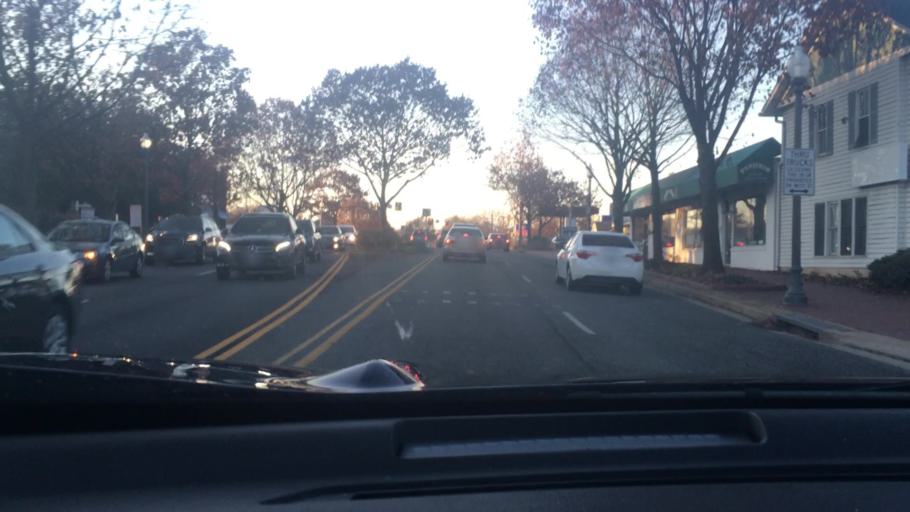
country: US
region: Virginia
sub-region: City of Falls Church
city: Falls Church
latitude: 38.8900
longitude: -77.1831
